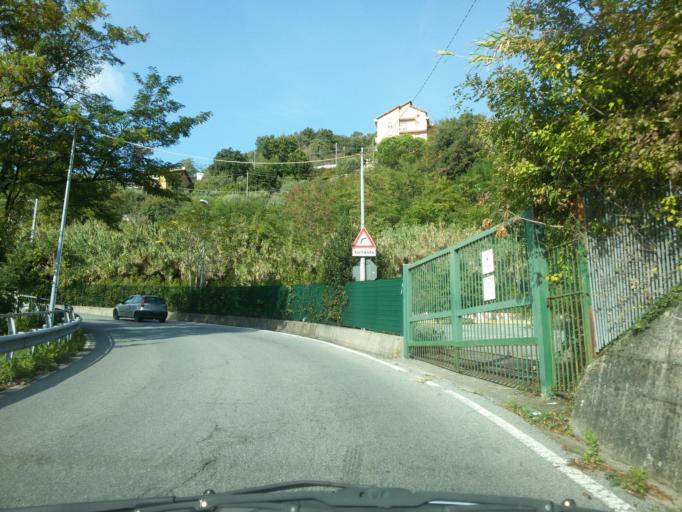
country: IT
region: Liguria
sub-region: Provincia di Genova
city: Piccarello
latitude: 44.4861
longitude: 8.9749
